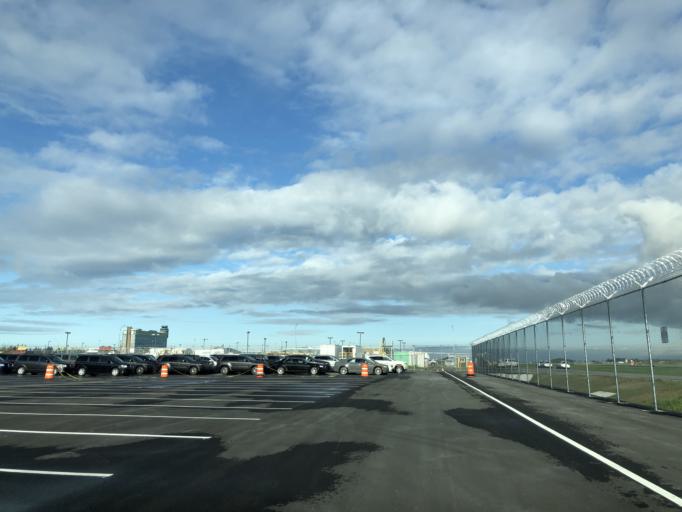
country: CA
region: British Columbia
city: Richmond
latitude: 49.1978
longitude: -123.1627
